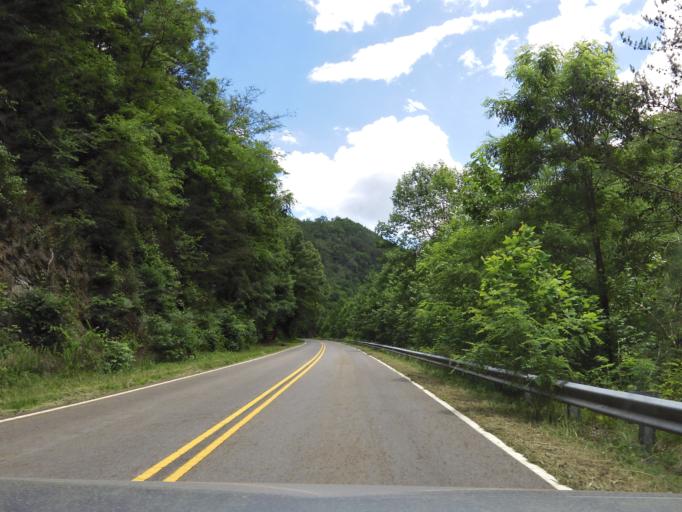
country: US
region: North Carolina
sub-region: Graham County
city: Robbinsville
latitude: 35.4402
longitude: -83.9333
